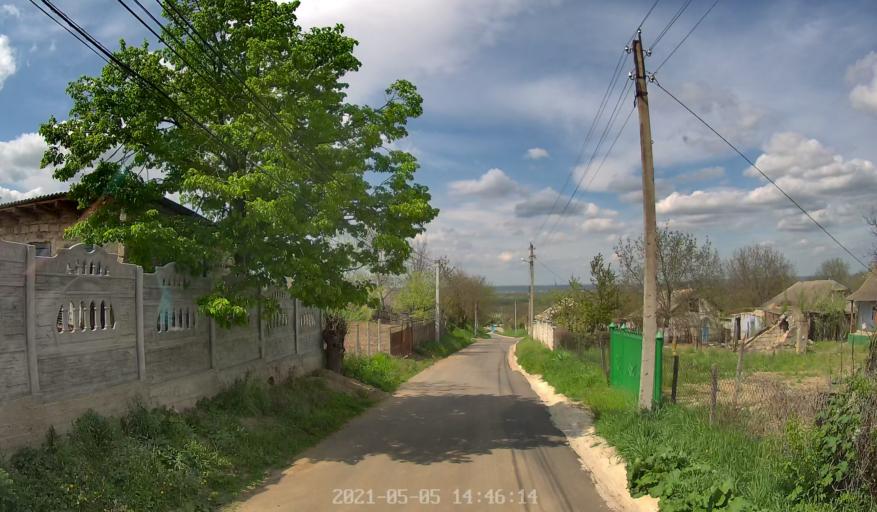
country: MD
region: Chisinau
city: Vadul lui Voda
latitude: 47.0928
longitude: 29.1735
